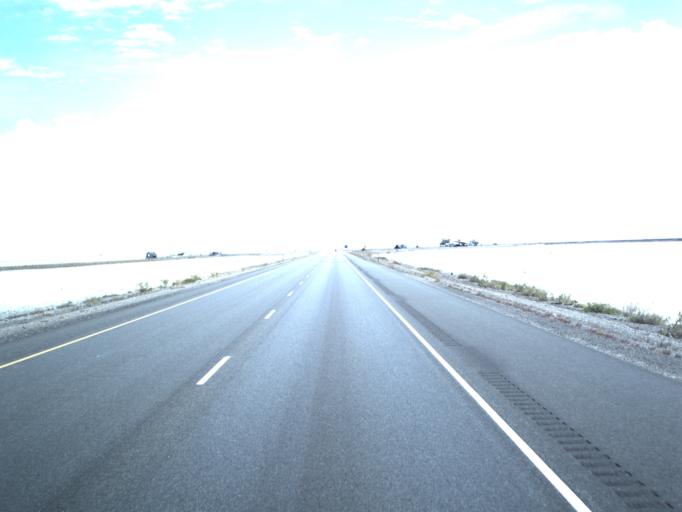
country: US
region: Utah
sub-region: Tooele County
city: Wendover
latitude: 40.7388
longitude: -113.8674
